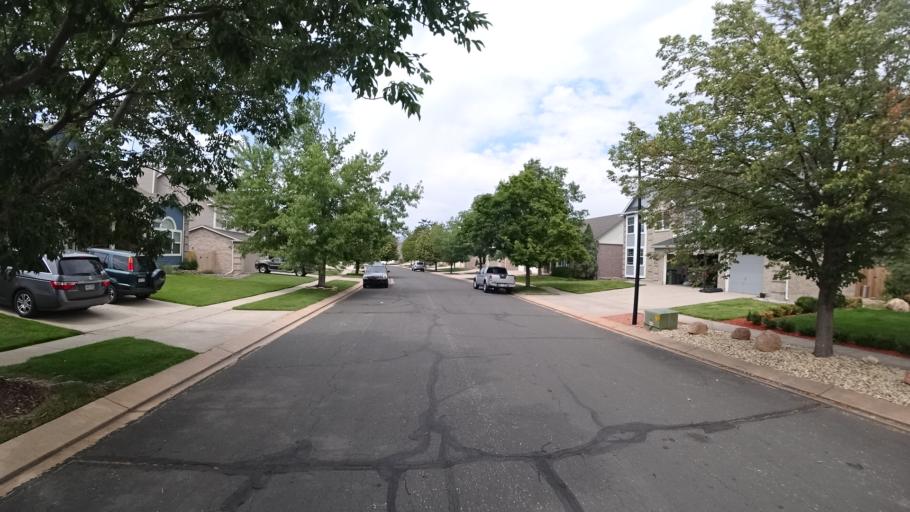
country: US
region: Colorado
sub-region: El Paso County
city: Air Force Academy
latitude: 38.9606
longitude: -104.7778
